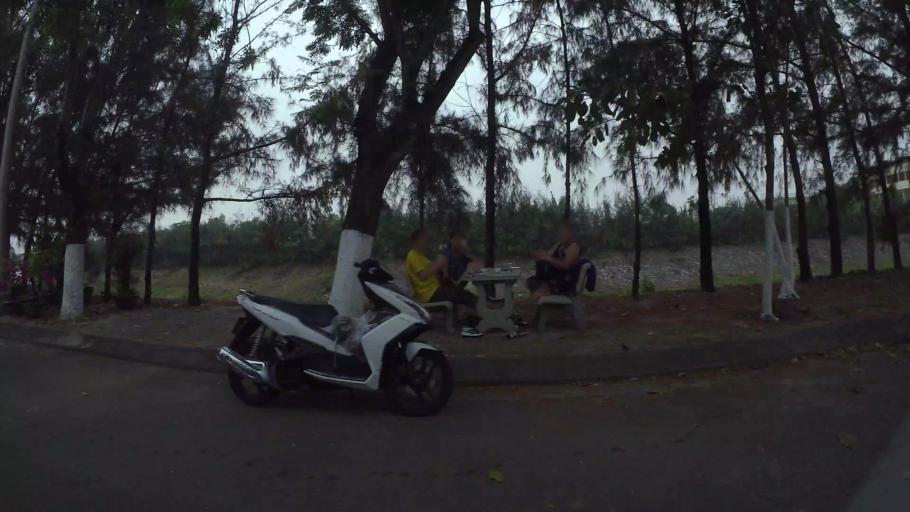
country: VN
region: Da Nang
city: Cam Le
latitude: 16.0304
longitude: 108.2158
